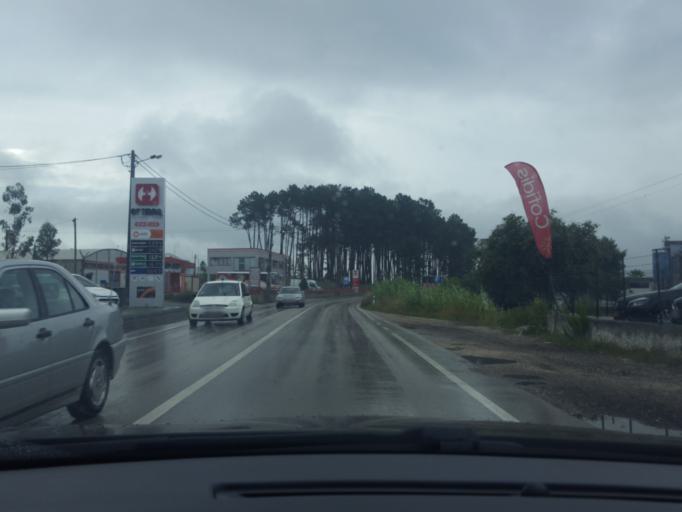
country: PT
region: Leiria
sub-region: Leiria
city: Leiria
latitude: 39.7351
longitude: -8.7649
